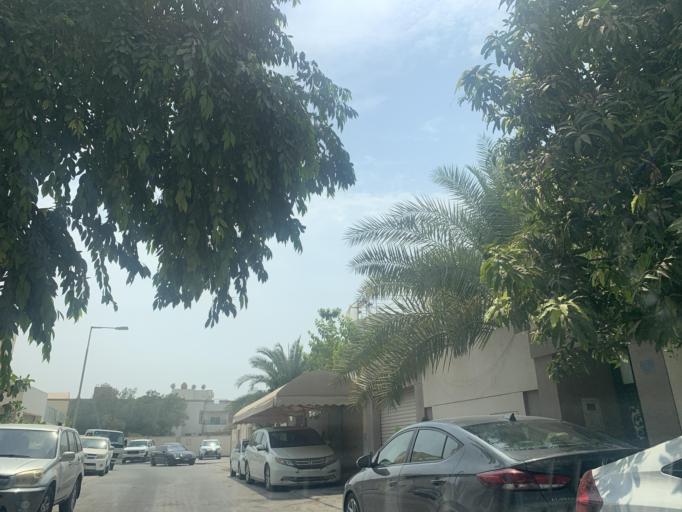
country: BH
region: Manama
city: Jidd Hafs
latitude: 26.2108
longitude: 50.5067
